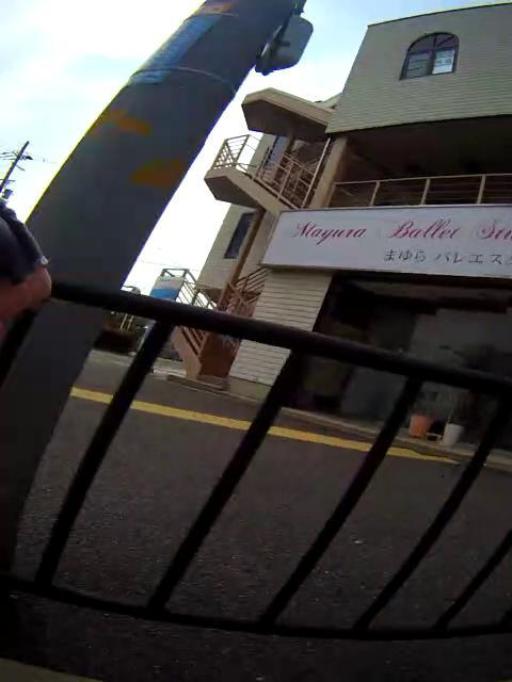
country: JP
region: Osaka
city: Toyonaka
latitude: 34.7939
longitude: 135.4727
